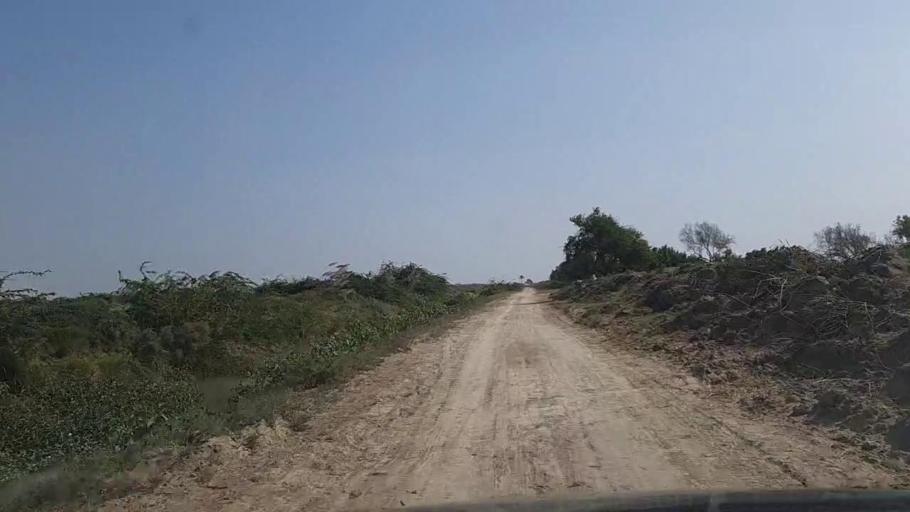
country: PK
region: Sindh
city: Gharo
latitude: 24.7152
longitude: 67.5725
